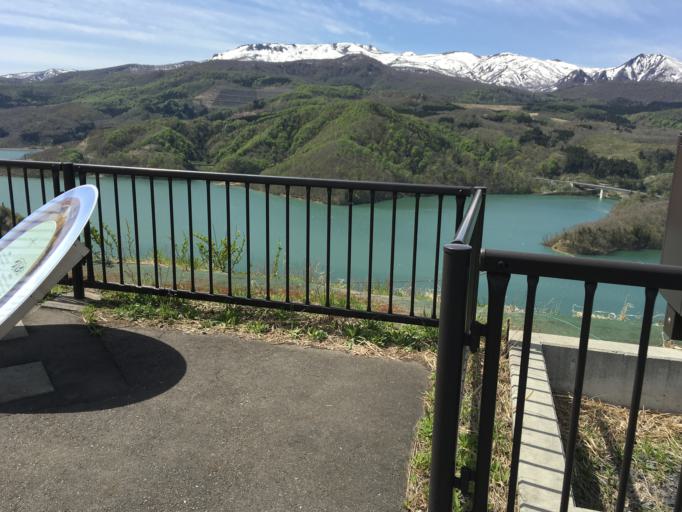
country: JP
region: Iwate
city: Mizusawa
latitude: 39.1158
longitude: 140.9198
